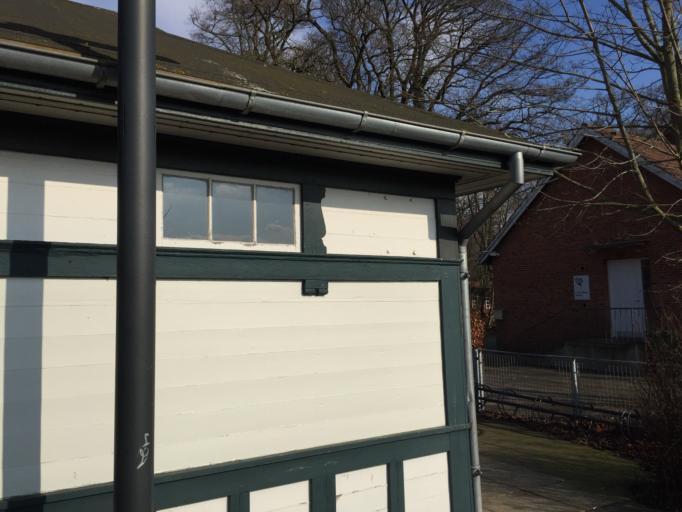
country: DK
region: South Denmark
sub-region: Odense Kommune
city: Odense
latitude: 55.3694
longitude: 10.3779
